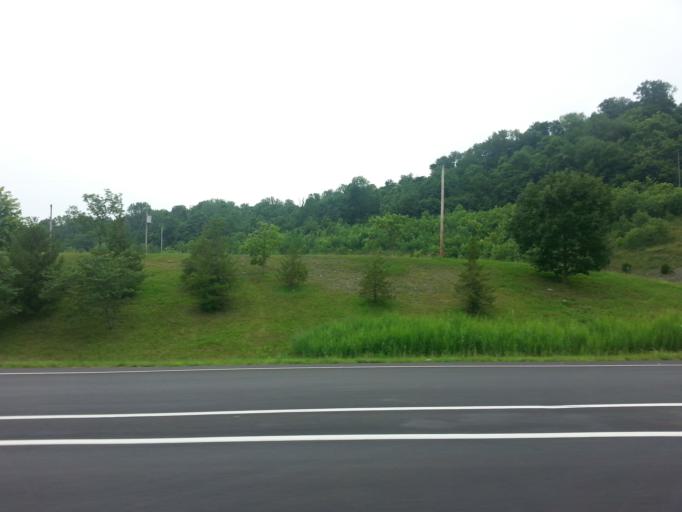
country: US
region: Ohio
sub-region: Brown County
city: Aberdeen
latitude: 38.6830
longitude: -83.7887
